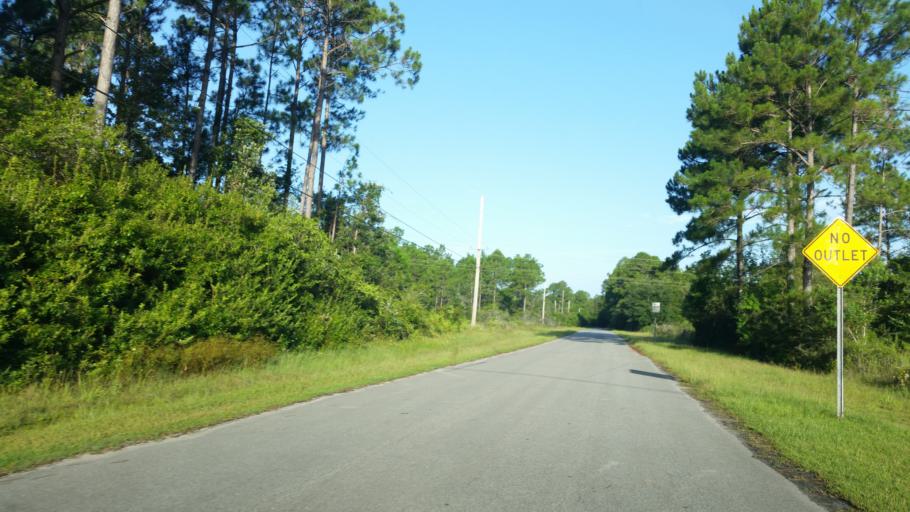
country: US
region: Florida
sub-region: Escambia County
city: Myrtle Grove
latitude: 30.4068
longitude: -87.3247
